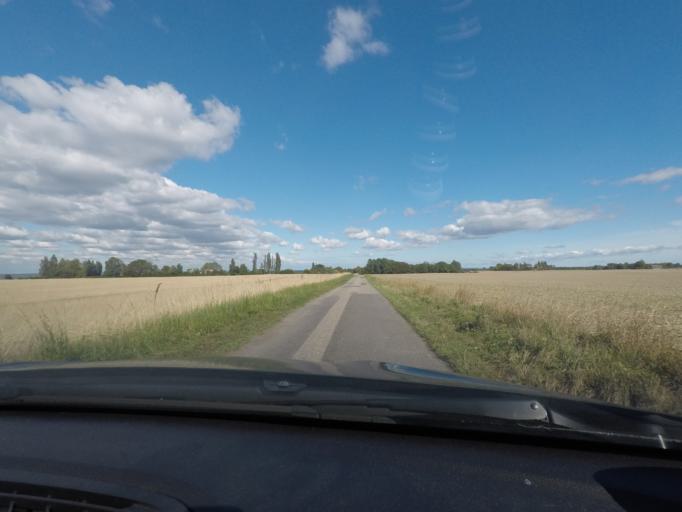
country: DK
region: Zealand
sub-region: Guldborgsund Kommune
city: Sakskobing
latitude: 54.9829
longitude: 11.5406
